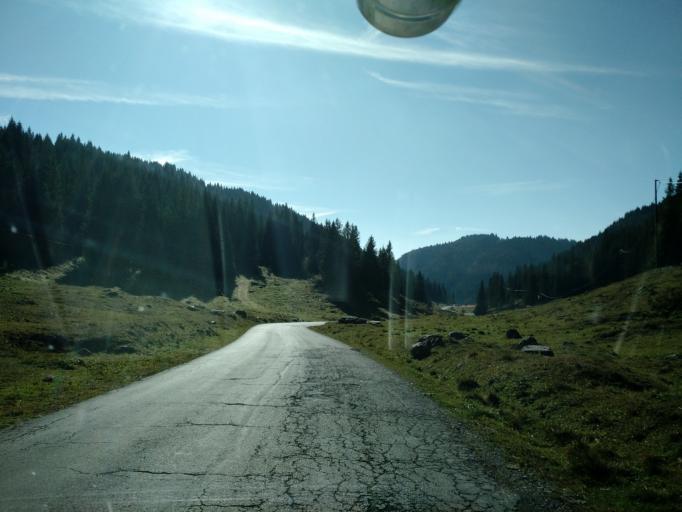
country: IT
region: Veneto
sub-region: Provincia di Vicenza
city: Gallio
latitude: 45.9300
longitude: 11.5598
